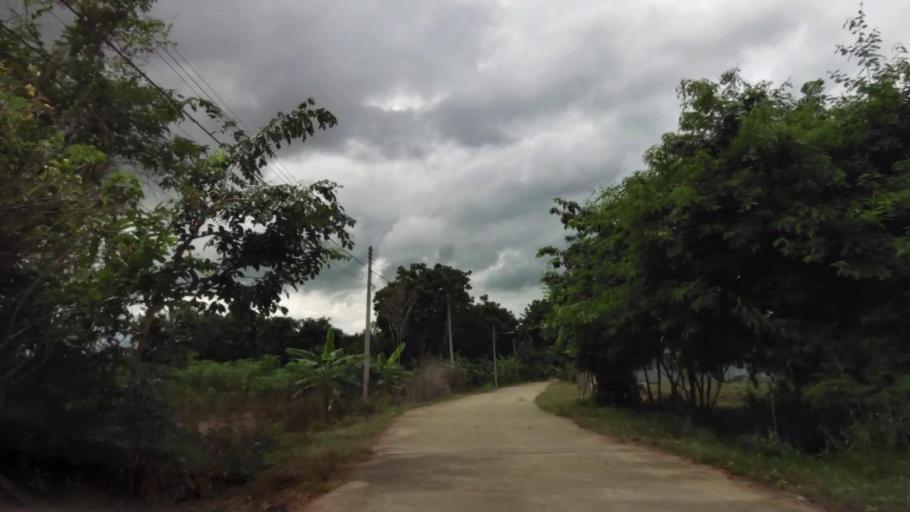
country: TH
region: Nakhon Sawan
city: Phai Sali
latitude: 15.6039
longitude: 100.6615
